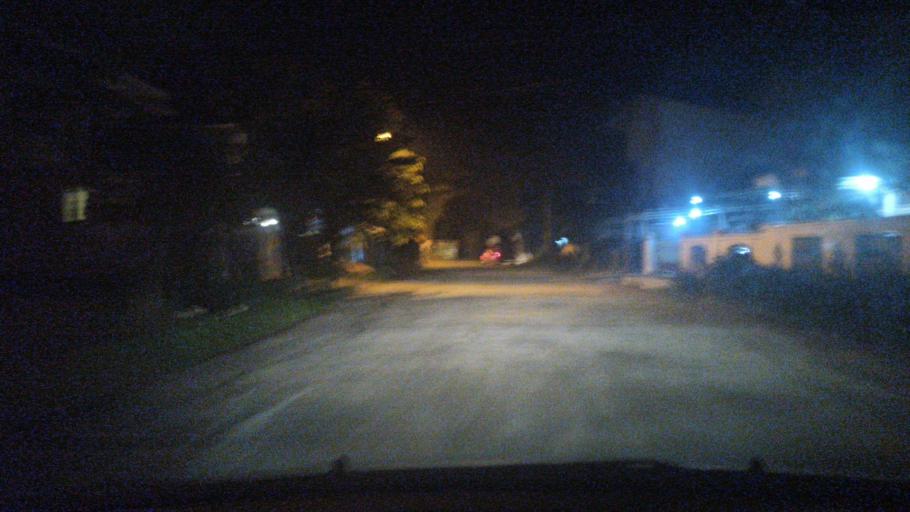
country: ID
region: South Sumatra
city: Plaju
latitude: -3.0085
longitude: 104.7133
